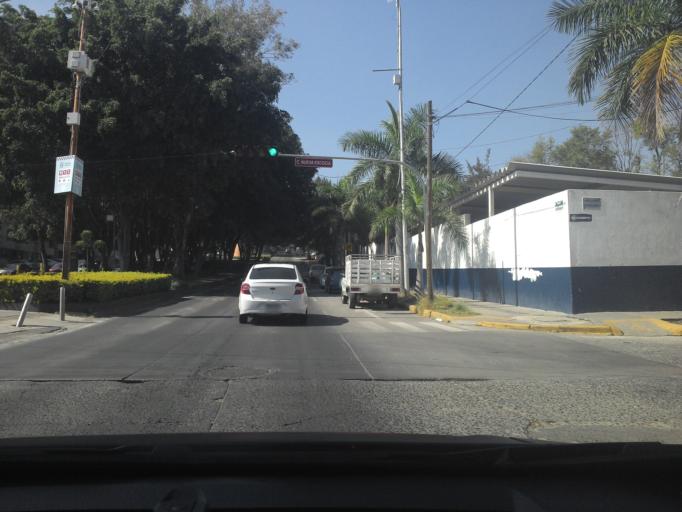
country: MX
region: Jalisco
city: Zapopan2
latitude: 20.6970
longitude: -103.3913
